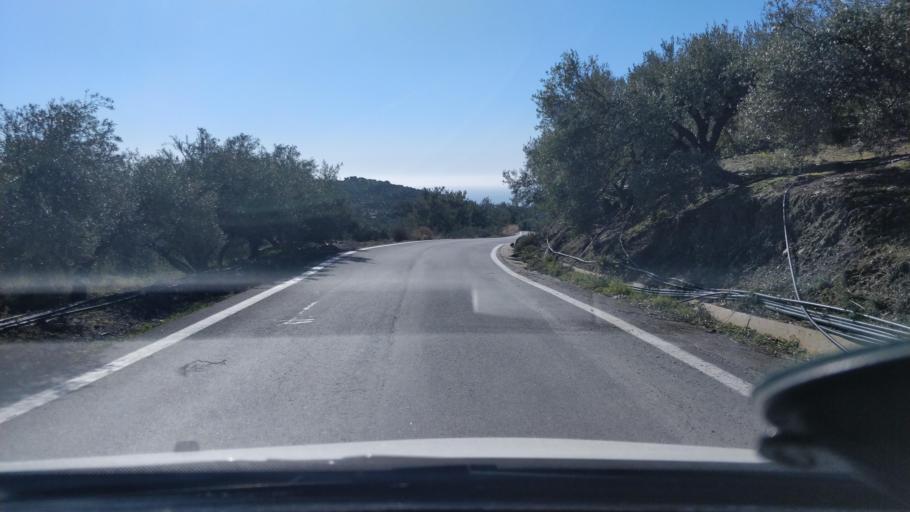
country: GR
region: Crete
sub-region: Nomos Irakleiou
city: Kastelli
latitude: 35.0245
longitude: 25.4487
